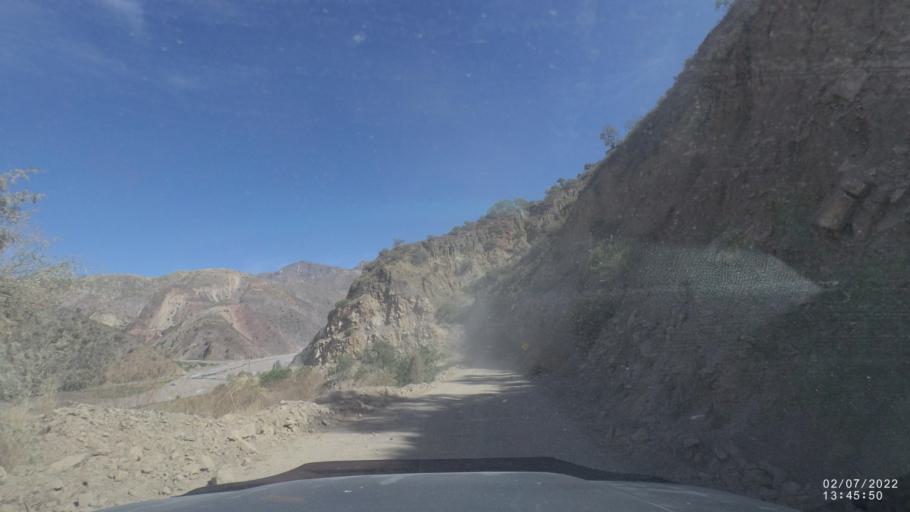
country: BO
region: Cochabamba
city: Irpa Irpa
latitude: -17.8108
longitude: -66.3651
